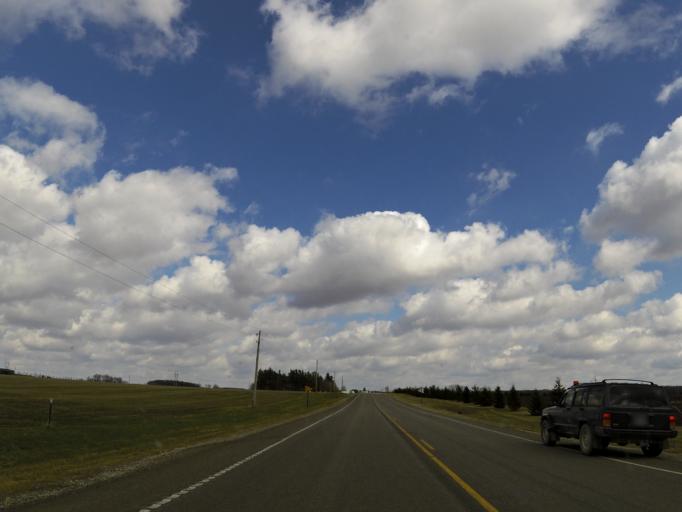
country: US
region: Minnesota
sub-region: Olmsted County
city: Byron
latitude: 44.0831
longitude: -92.6832
